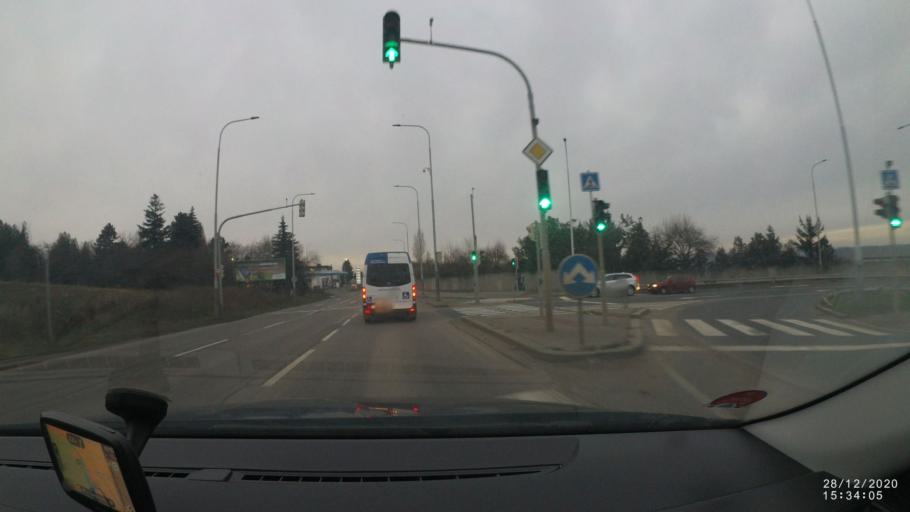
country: CZ
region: Praha
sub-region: Praha 9
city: Vysocany
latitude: 50.0928
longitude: 14.5293
